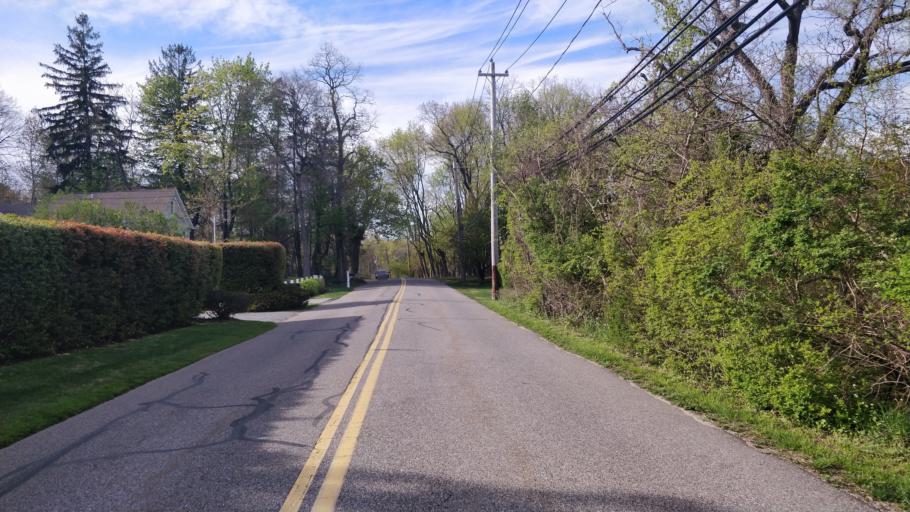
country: US
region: New York
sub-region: Suffolk County
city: East Setauket
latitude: 40.9574
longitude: -73.1280
